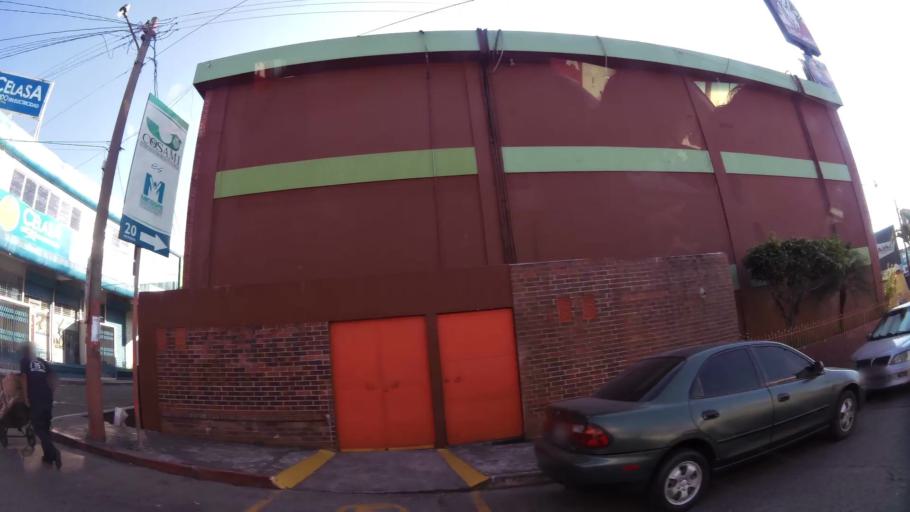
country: GT
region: Suchitepeque
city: Mazatenango
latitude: 14.5341
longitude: -91.5085
